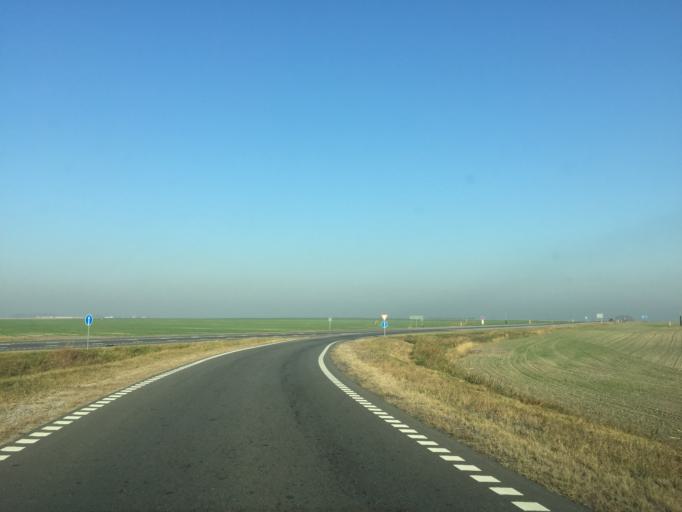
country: BY
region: Gomel
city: Kastsyukowka
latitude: 52.4914
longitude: 30.8192
